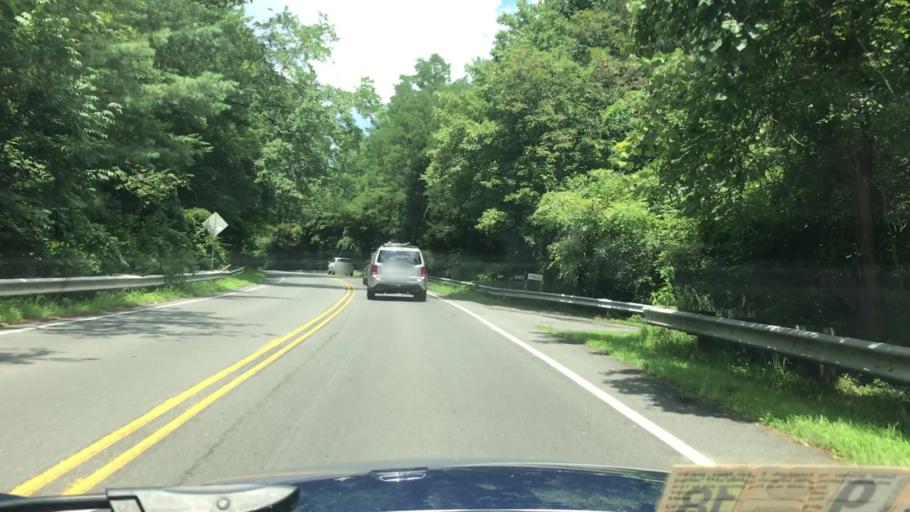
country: US
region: Virginia
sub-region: Fairfax County
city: Wolf Trap
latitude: 38.9190
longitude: -77.3032
